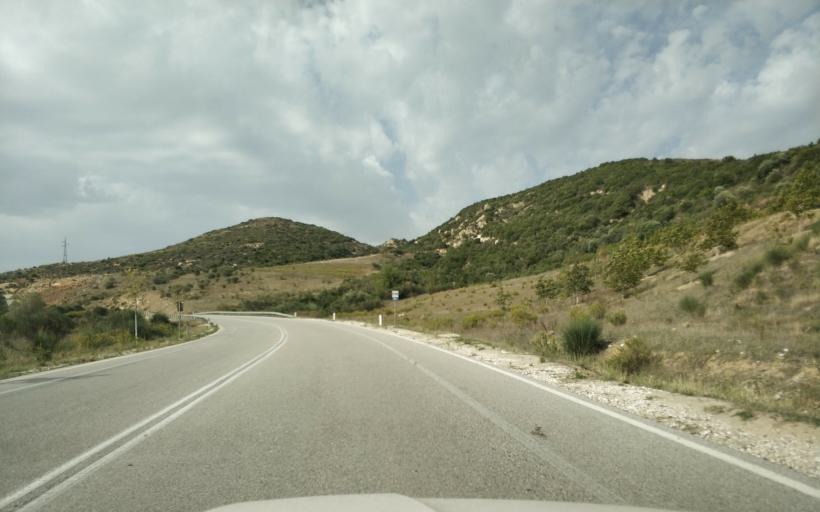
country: AL
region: Gjirokaster
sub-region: Rrethi i Tepelenes
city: Krahes
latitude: 40.3952
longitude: 19.8718
